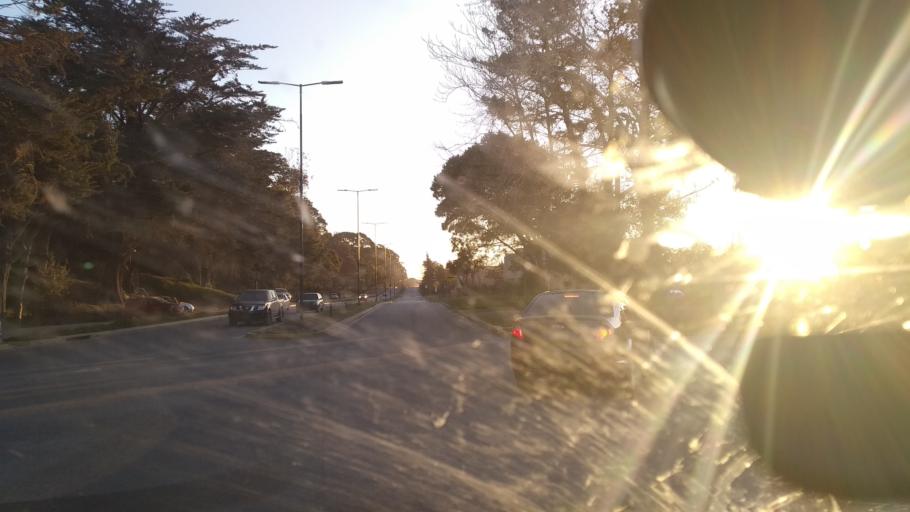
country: AR
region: Buenos Aires
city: Necochea
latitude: -38.5842
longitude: -58.7471
